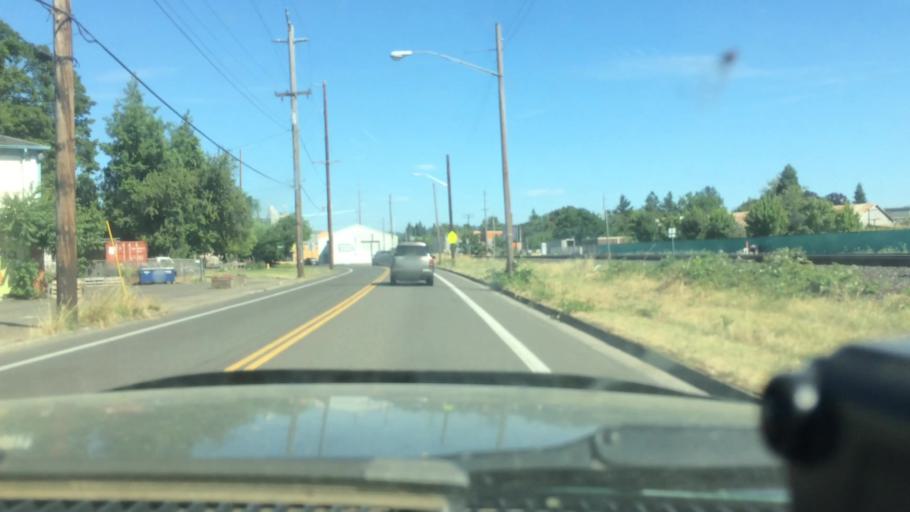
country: US
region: Oregon
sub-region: Lane County
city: Eugene
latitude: 44.0594
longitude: -123.1117
